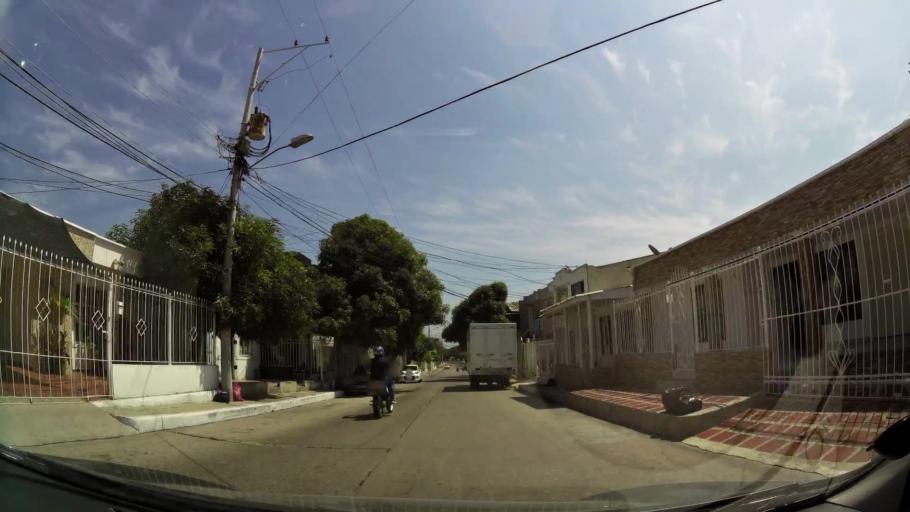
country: CO
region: Atlantico
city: Barranquilla
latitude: 10.9632
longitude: -74.8022
